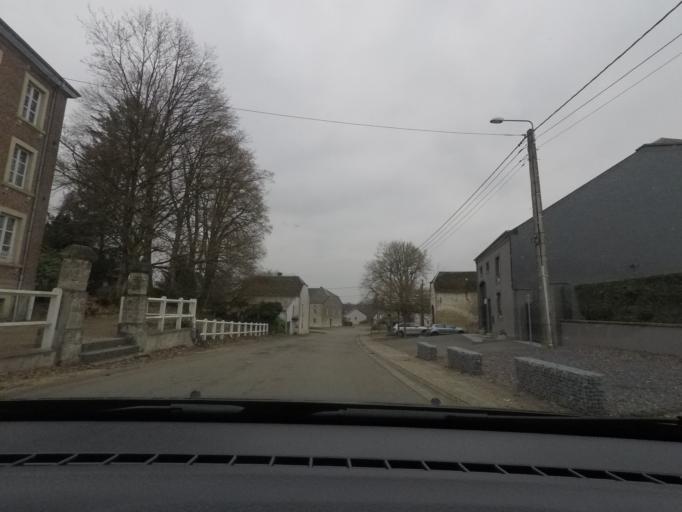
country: BE
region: Wallonia
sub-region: Province du Luxembourg
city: Etalle
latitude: 49.7067
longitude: 5.5869
